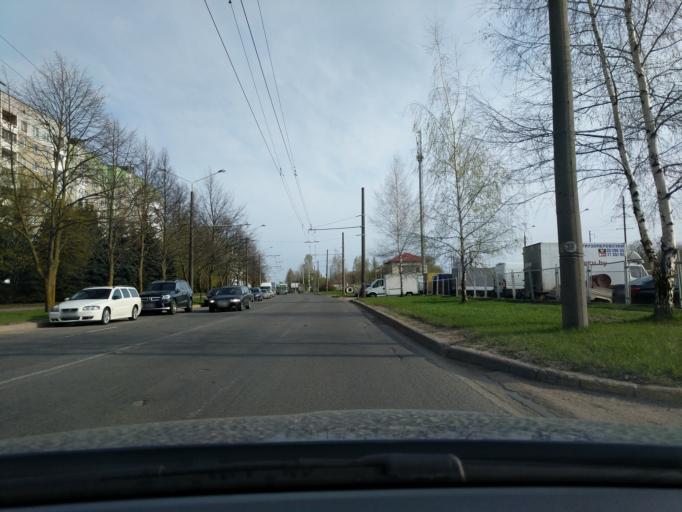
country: BY
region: Minsk
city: Novoye Medvezhino
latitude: 53.9013
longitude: 27.4632
